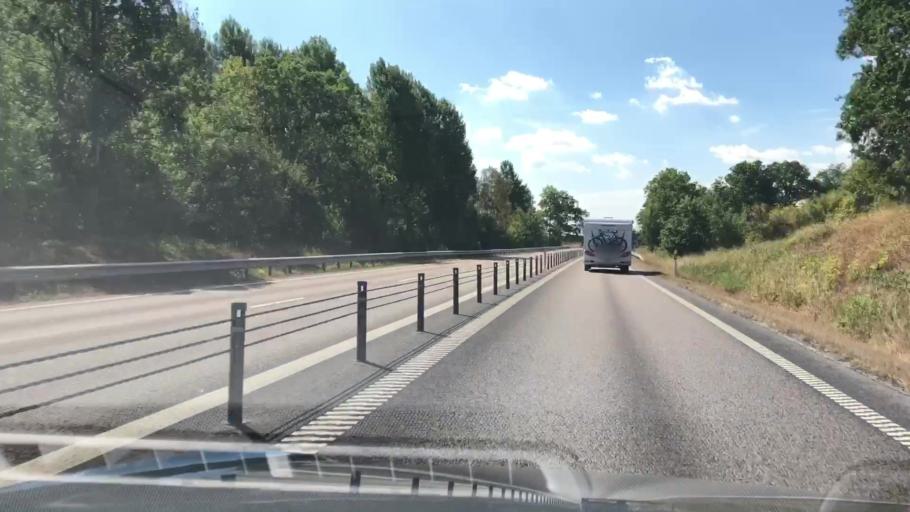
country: SE
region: Kalmar
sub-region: Kalmar Kommun
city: Lindsdal
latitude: 56.8152
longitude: 16.3694
